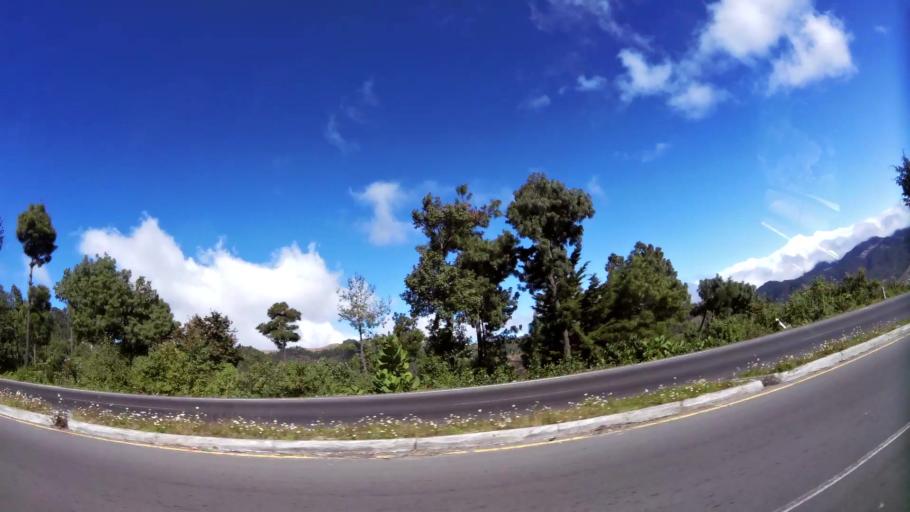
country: GT
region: Solola
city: Santa Catarina Ixtahuacan
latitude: 14.8248
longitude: -91.3449
